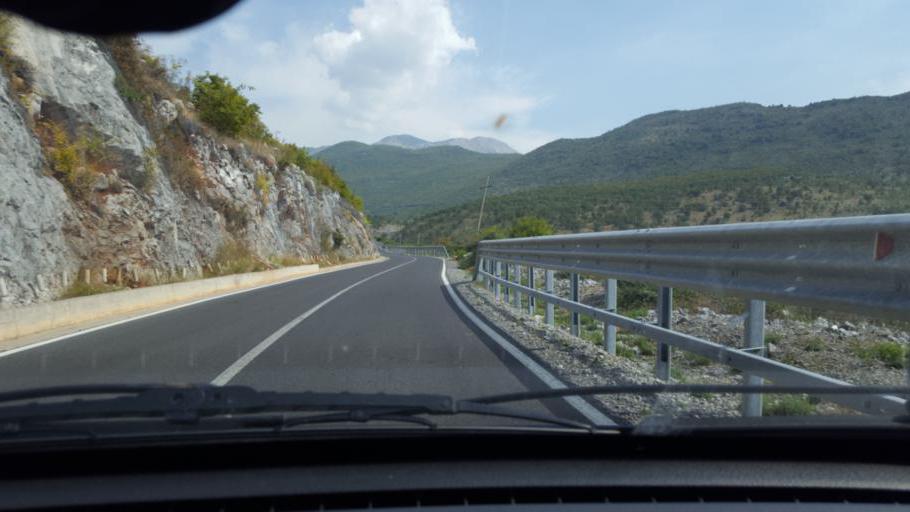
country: AL
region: Shkoder
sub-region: Rrethi i Malesia e Madhe
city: Hot
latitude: 42.3742
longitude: 19.4588
